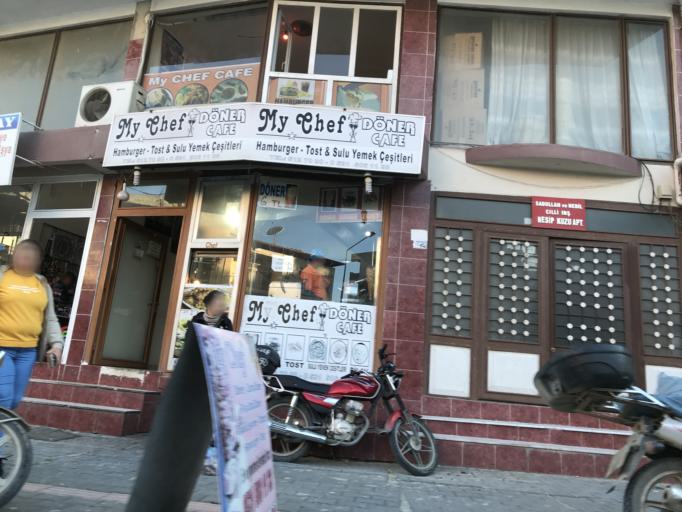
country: TR
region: Hatay
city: Samandag
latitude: 36.0830
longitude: 35.9895
